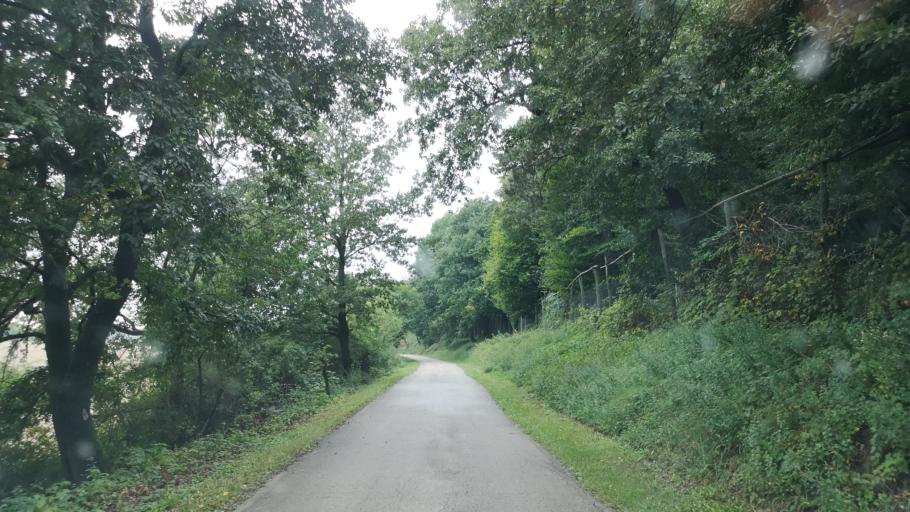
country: SK
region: Trnavsky
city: Smolenice
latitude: 48.5735
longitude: 17.4172
